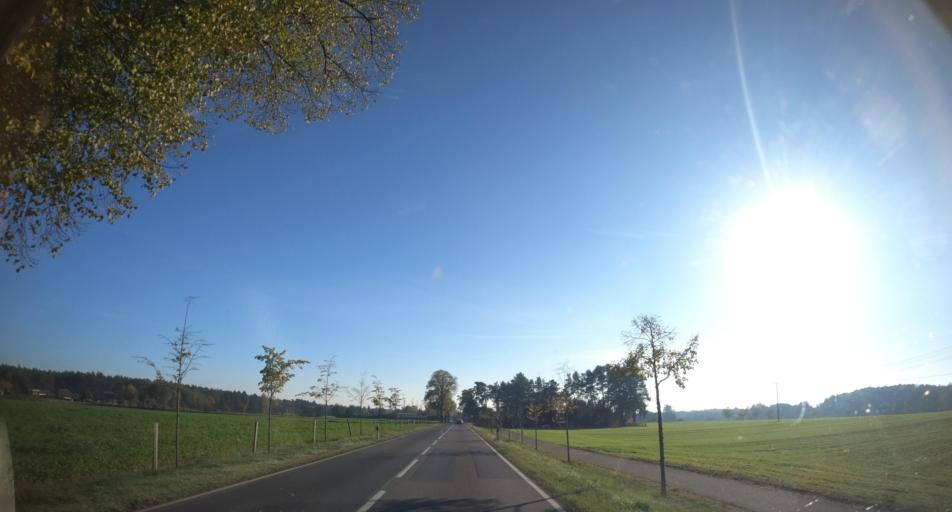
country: DE
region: Mecklenburg-Vorpommern
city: Eggesin
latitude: 53.7113
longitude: 14.0685
